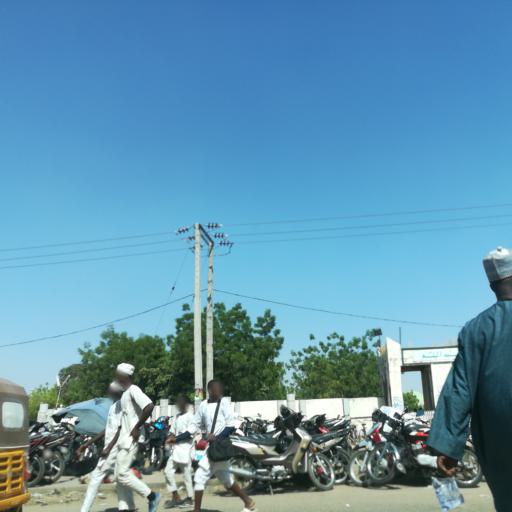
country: NG
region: Kano
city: Kano
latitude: 12.0007
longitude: 8.5269
